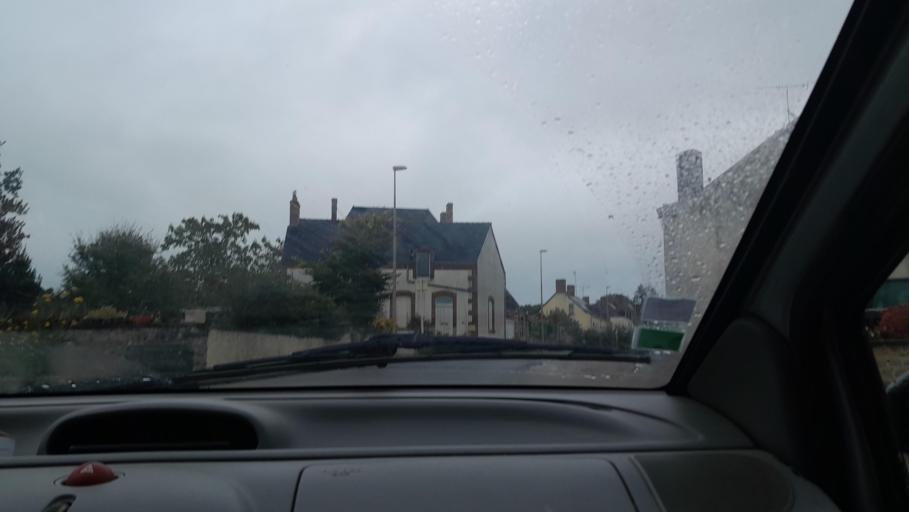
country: FR
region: Pays de la Loire
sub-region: Departement de la Mayenne
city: Congrier
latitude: 47.8792
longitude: -1.1282
